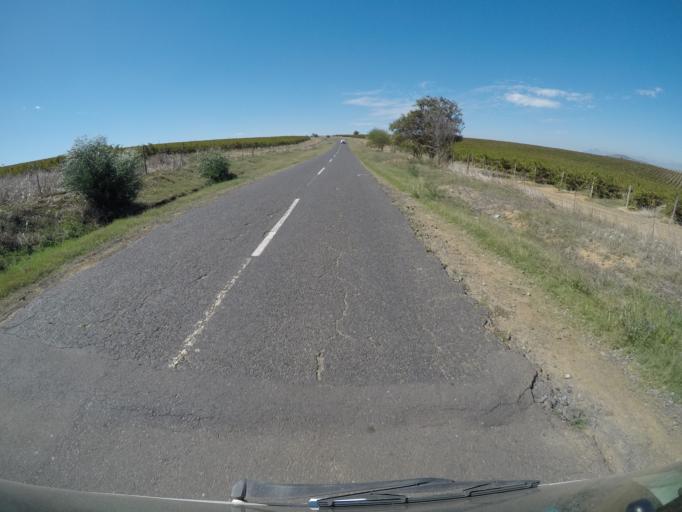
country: ZA
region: Western Cape
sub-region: City of Cape Town
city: Sunset Beach
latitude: -33.7181
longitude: 18.5786
